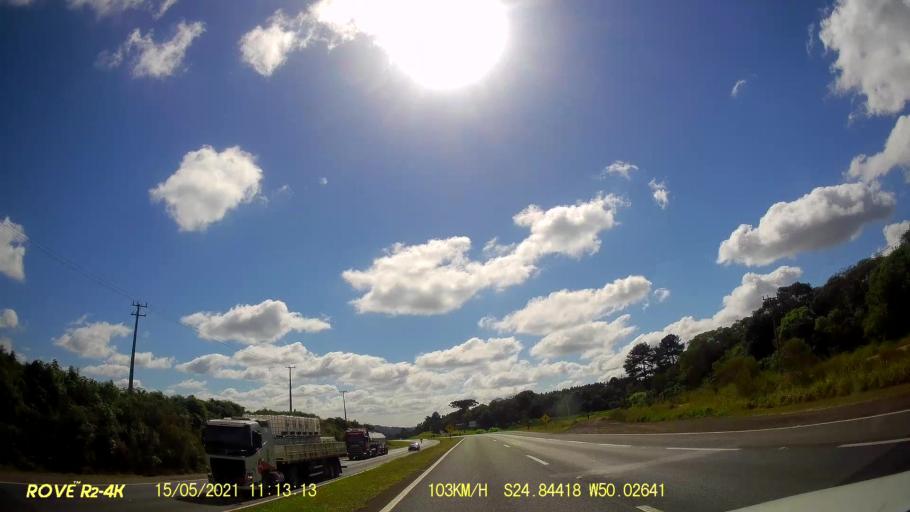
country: BR
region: Parana
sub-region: Castro
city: Castro
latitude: -24.8443
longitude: -50.0265
